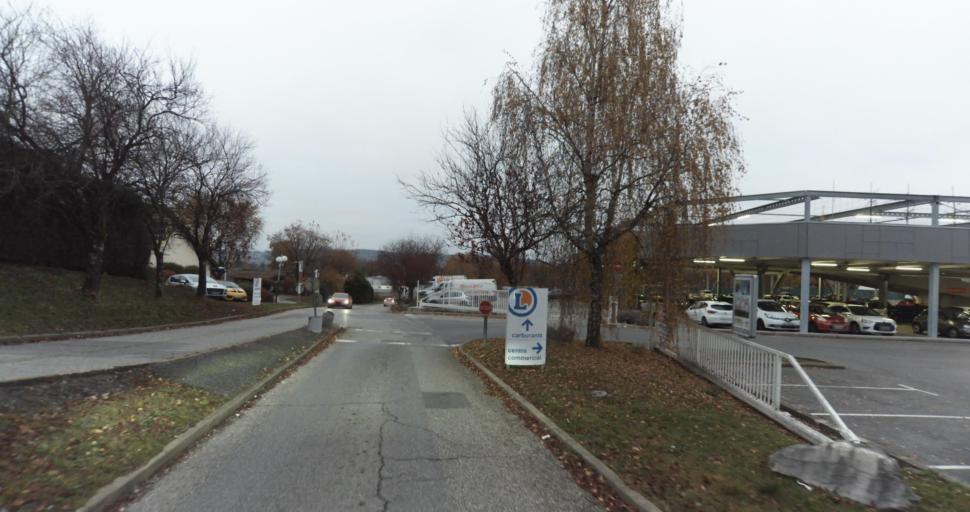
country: FR
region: Rhone-Alpes
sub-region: Departement de la Haute-Savoie
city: Seynod
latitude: 45.8921
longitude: 6.0908
